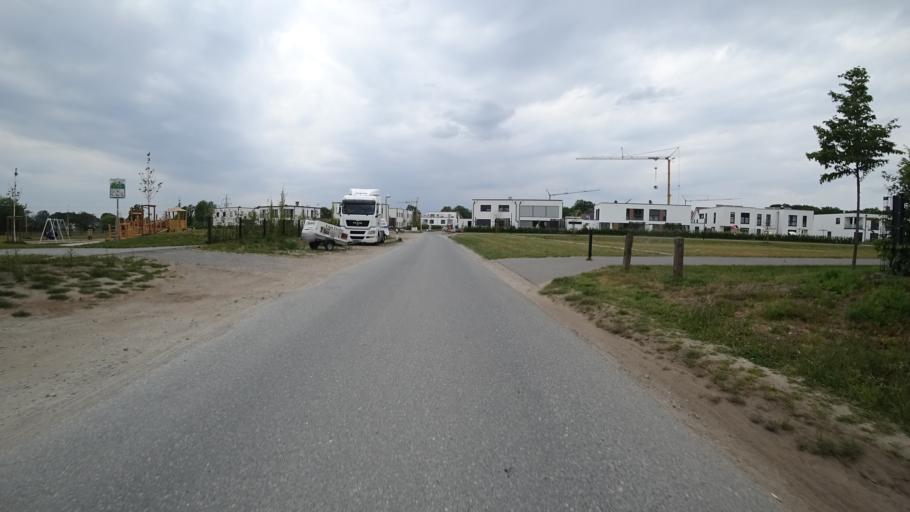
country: DE
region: North Rhine-Westphalia
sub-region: Regierungsbezirk Detmold
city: Guetersloh
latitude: 51.9057
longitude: 8.3458
